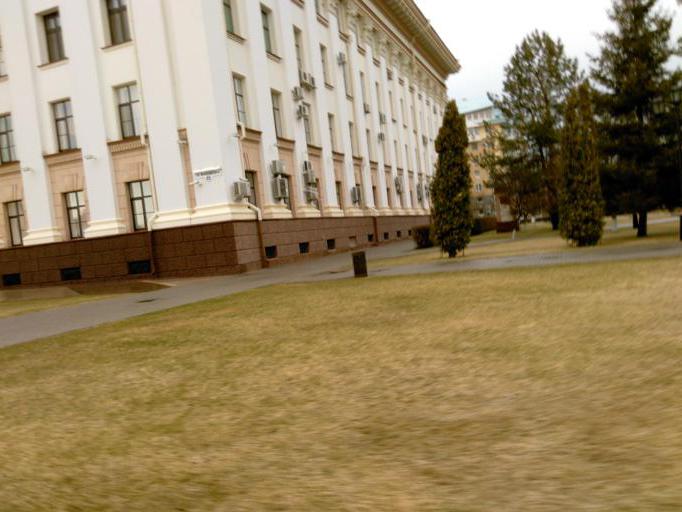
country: RU
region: Tjumen
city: Tyumen
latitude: 57.1537
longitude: 65.5435
